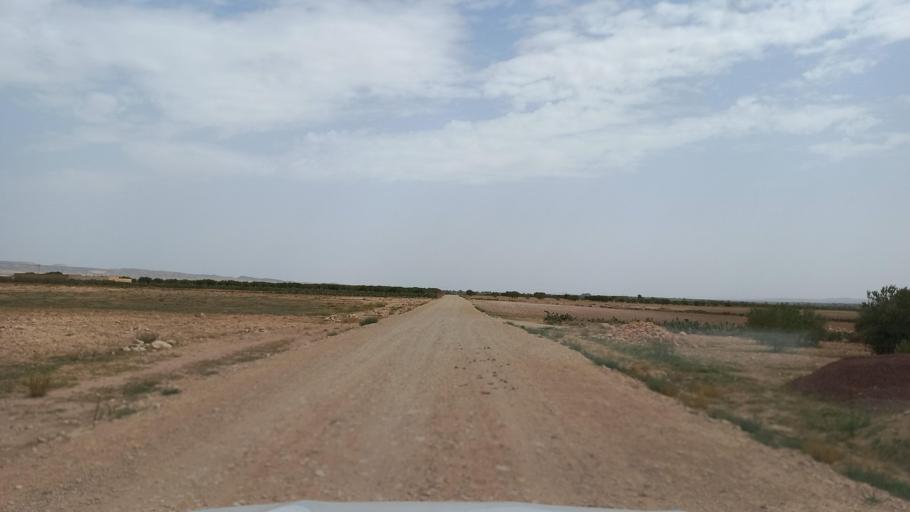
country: TN
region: Al Qasrayn
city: Kasserine
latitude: 35.2809
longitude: 9.0104
